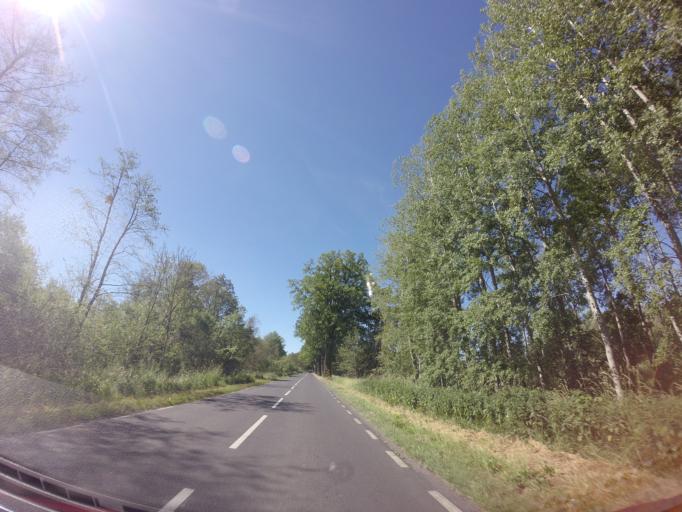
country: PL
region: West Pomeranian Voivodeship
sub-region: Powiat pyrzycki
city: Przelewice
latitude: 53.1636
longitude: 15.0397
